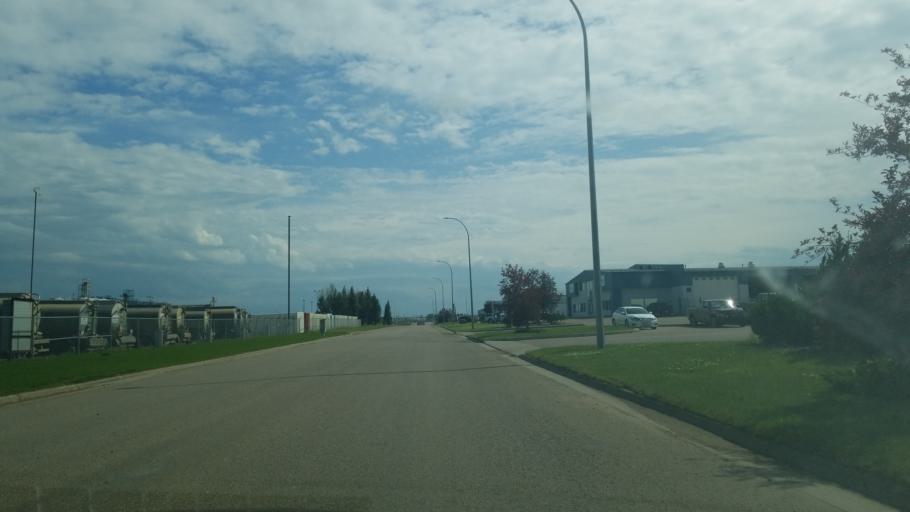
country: CA
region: Saskatchewan
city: Lloydminster
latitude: 53.2897
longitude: -110.0368
